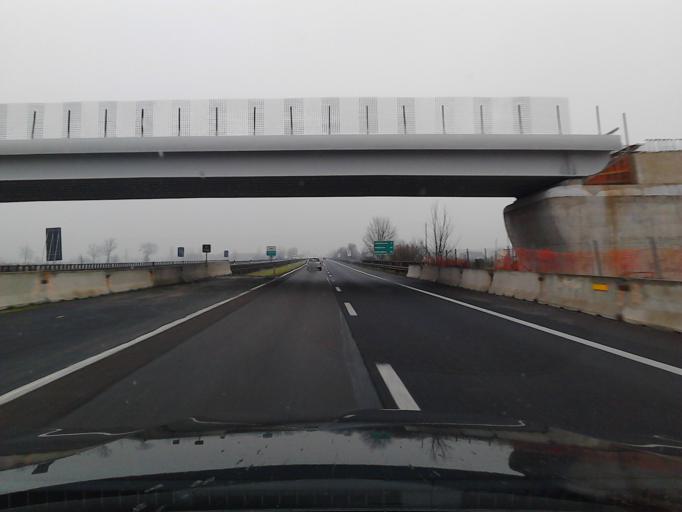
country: IT
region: Lombardy
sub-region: Provincia di Mantova
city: San Biagio
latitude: 45.0836
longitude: 10.8518
